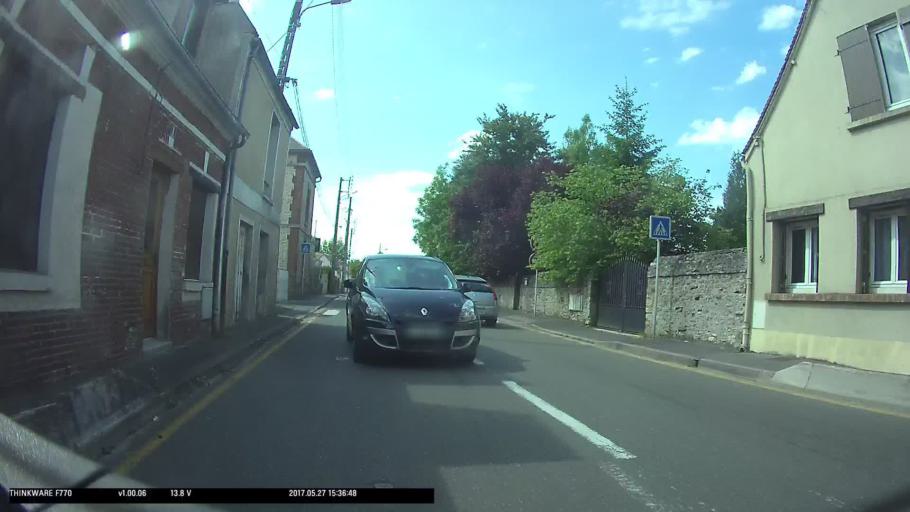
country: FR
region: Picardie
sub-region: Departement de l'Oise
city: Chaumont-en-Vexin
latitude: 49.2667
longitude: 1.8731
